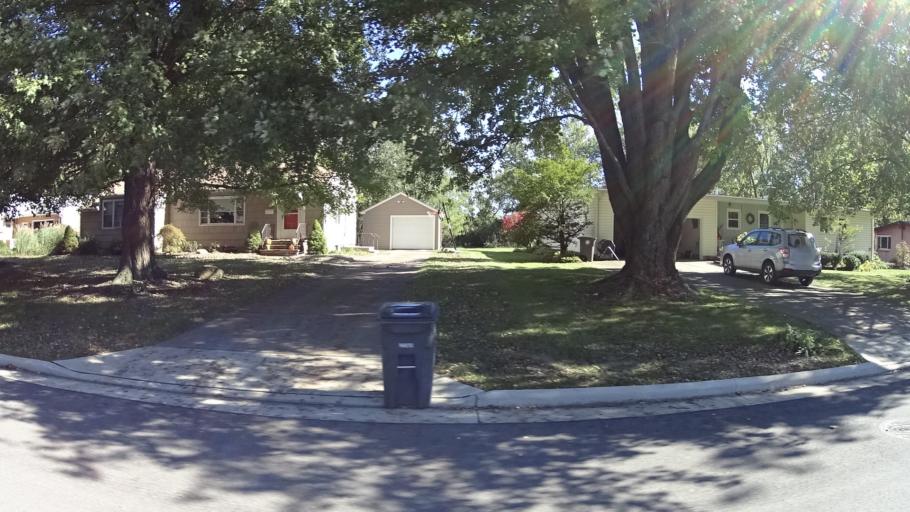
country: US
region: Ohio
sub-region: Lorain County
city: Oberlin
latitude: 41.2961
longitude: -82.2281
